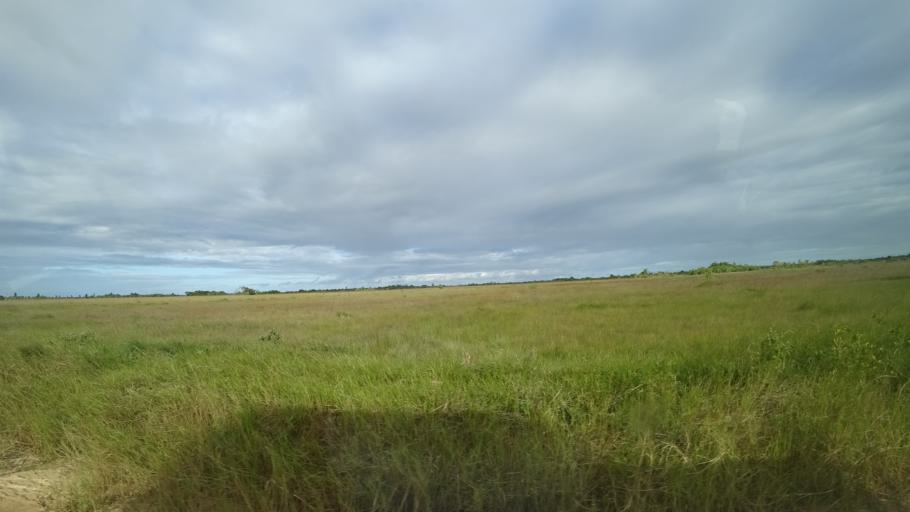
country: MZ
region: Sofala
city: Beira
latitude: -19.6943
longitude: 35.0361
